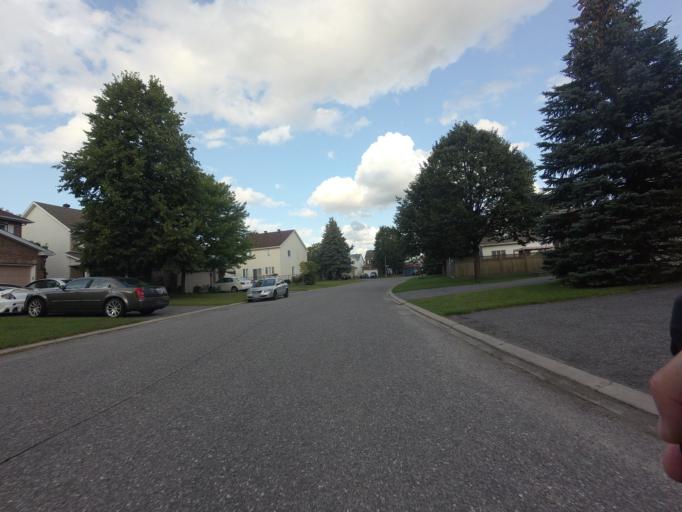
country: CA
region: Ontario
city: Bells Corners
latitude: 45.2848
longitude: -75.7174
